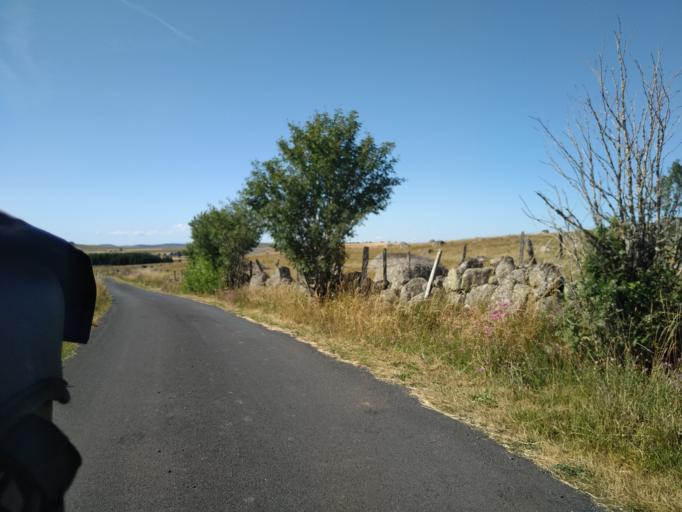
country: FR
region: Languedoc-Roussillon
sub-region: Departement de la Lozere
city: Aumont-Aubrac
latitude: 44.6765
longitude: 3.0975
